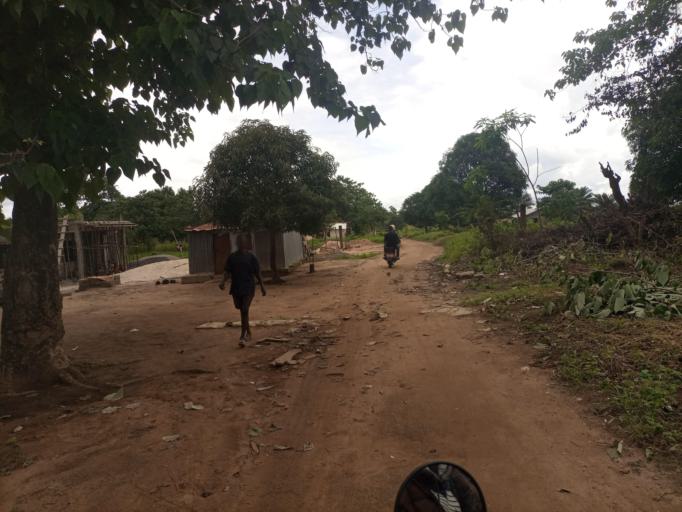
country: SL
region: Northern Province
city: Masoyila
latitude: 8.5694
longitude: -13.1598
